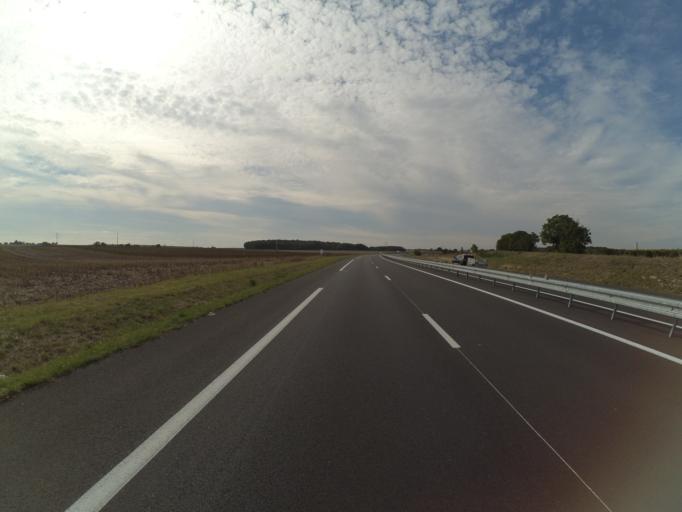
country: FR
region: Pays de la Loire
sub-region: Departement de Maine-et-Loire
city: Distre
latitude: 47.2111
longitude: -0.1846
